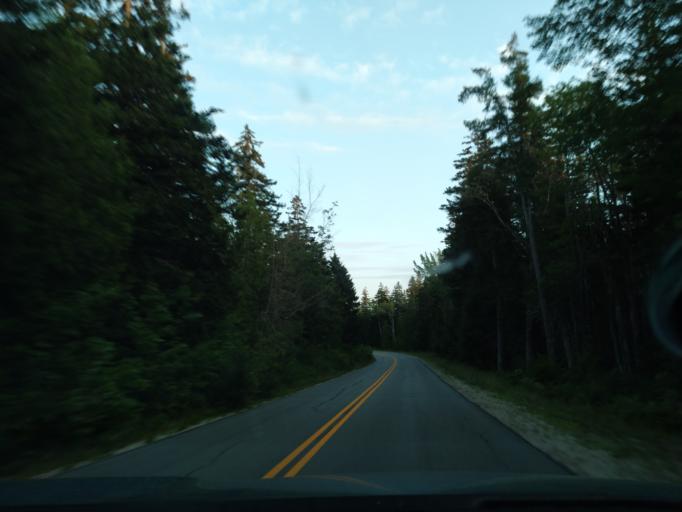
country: US
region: Maine
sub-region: Hancock County
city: Gouldsboro
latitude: 44.3913
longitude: -68.0732
